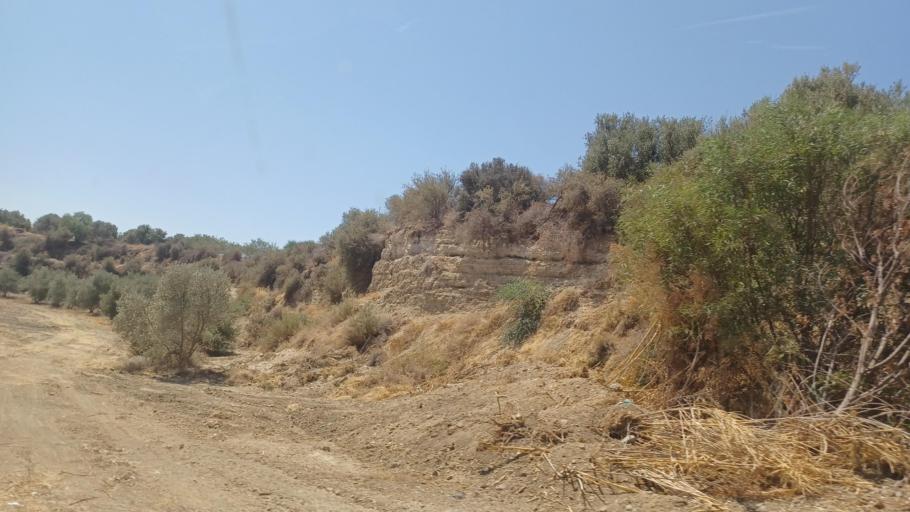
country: CY
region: Pafos
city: Polis
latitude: 35.0560
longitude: 32.4634
